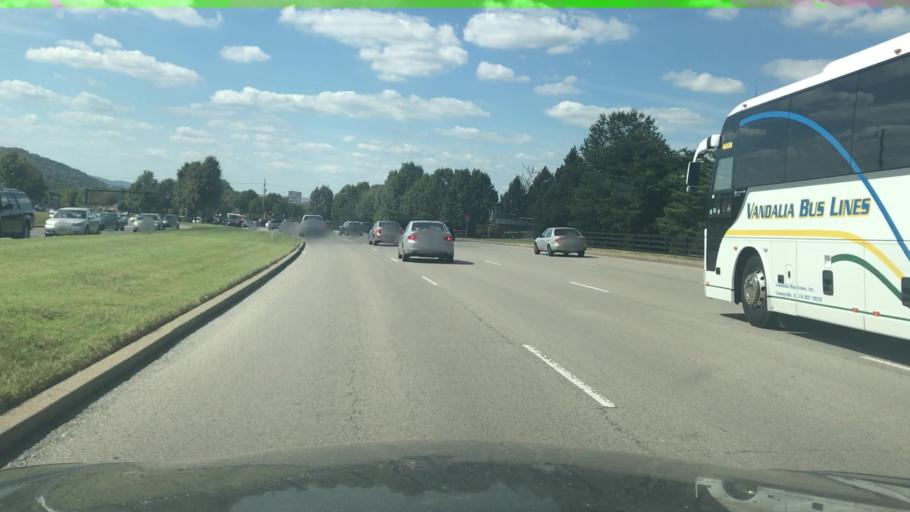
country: US
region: Tennessee
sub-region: Williamson County
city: Franklin
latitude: 35.9481
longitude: -86.8173
